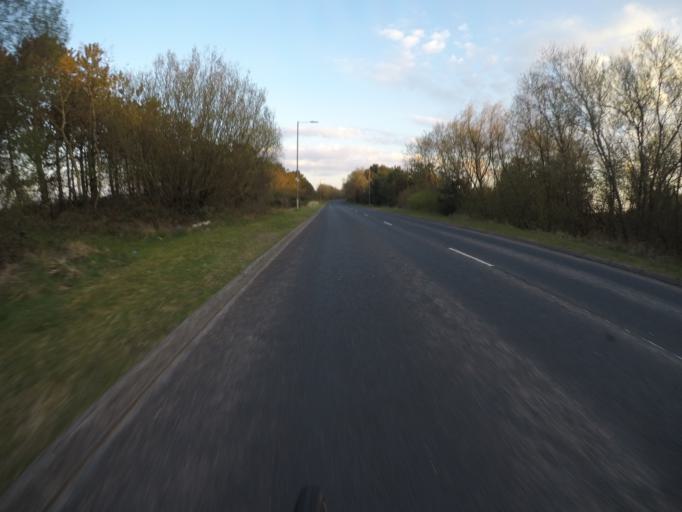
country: GB
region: Scotland
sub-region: North Ayrshire
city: Irvine
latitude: 55.5949
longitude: -4.6685
